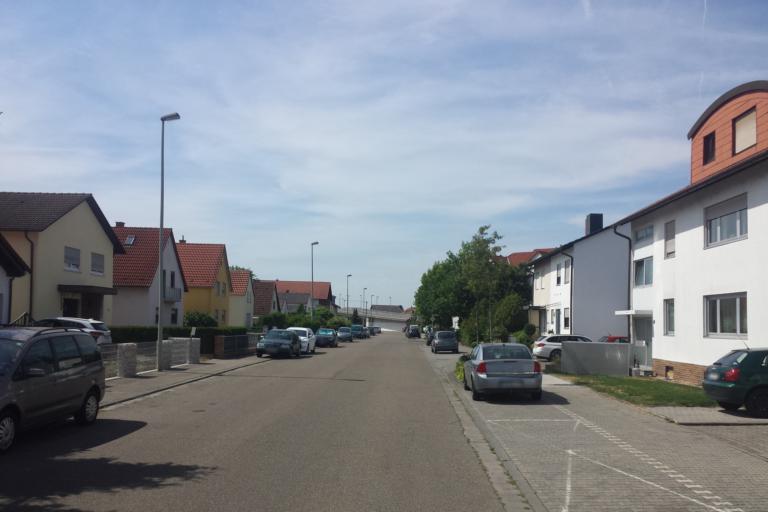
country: DE
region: Hesse
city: Lampertheim
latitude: 49.5863
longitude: 8.4857
